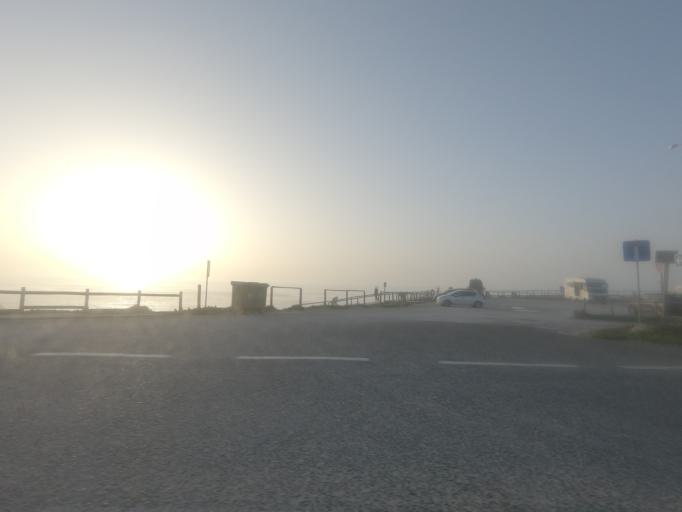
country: PT
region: Leiria
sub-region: Marinha Grande
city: Marinha Grande
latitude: 39.7686
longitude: -9.0284
